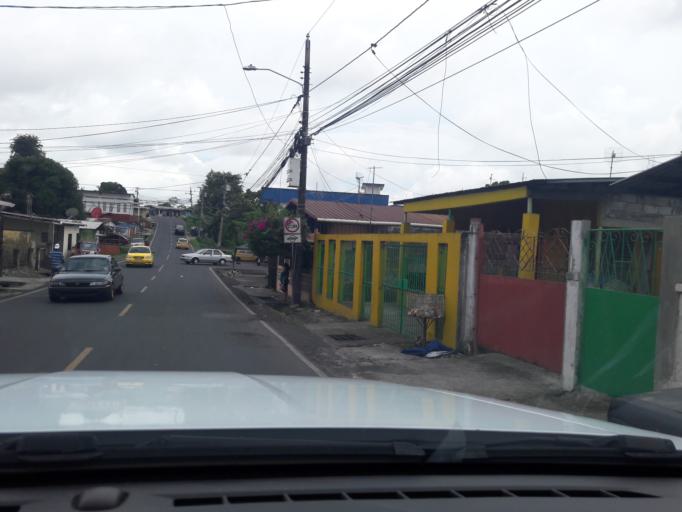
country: PA
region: Panama
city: San Miguelito
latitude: 9.0488
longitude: -79.5022
